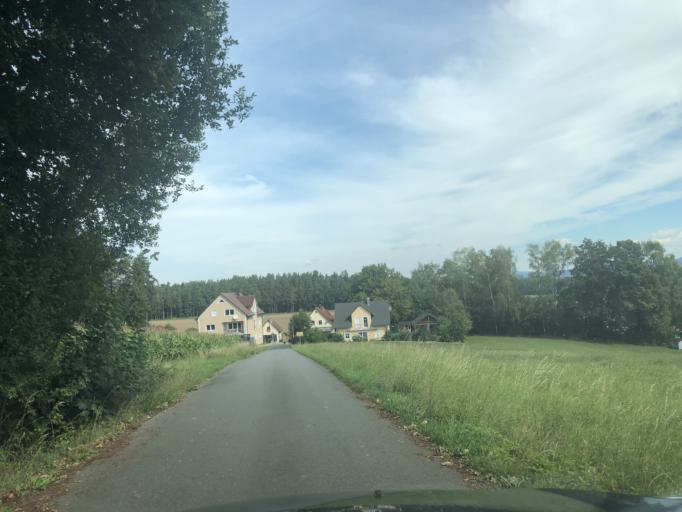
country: DE
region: Bavaria
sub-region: Upper Palatinate
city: Trabitz
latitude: 49.7995
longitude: 11.8658
